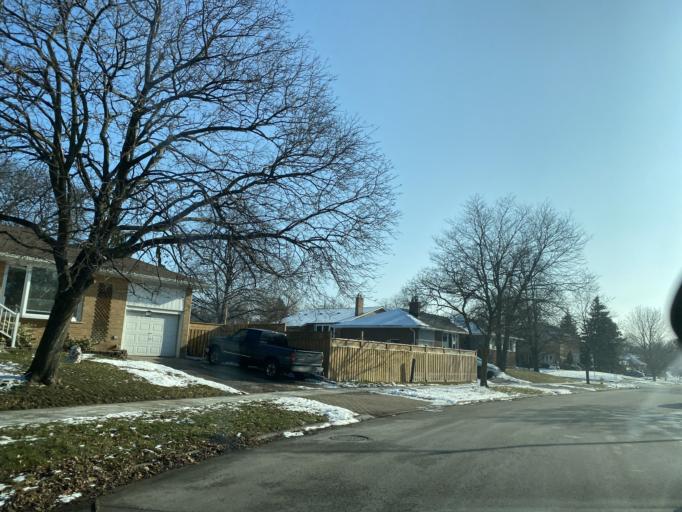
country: CA
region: Ontario
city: Etobicoke
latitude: 43.6646
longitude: -79.5696
